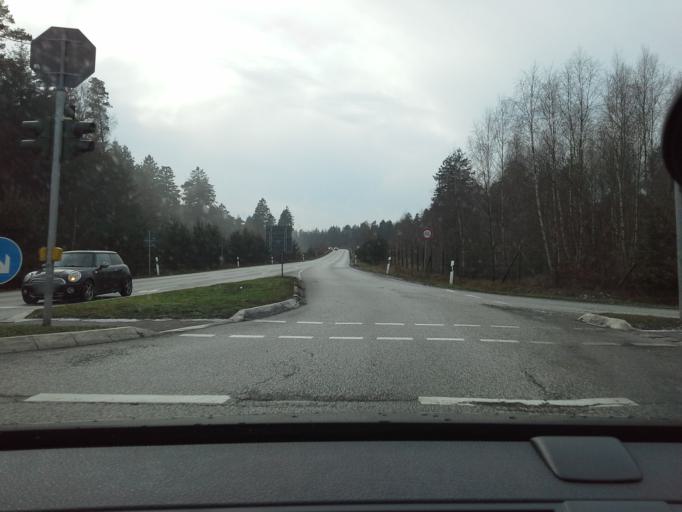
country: DE
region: Schleswig-Holstein
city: Henstedt-Ulzburg
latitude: 53.7479
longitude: 9.9918
